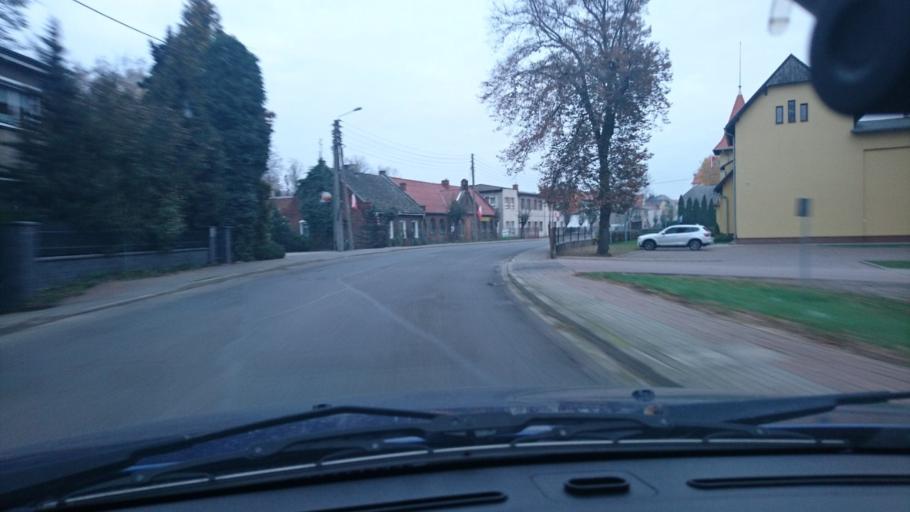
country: PL
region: Greater Poland Voivodeship
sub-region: Powiat ostrowski
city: Odolanow
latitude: 51.5732
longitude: 17.6685
